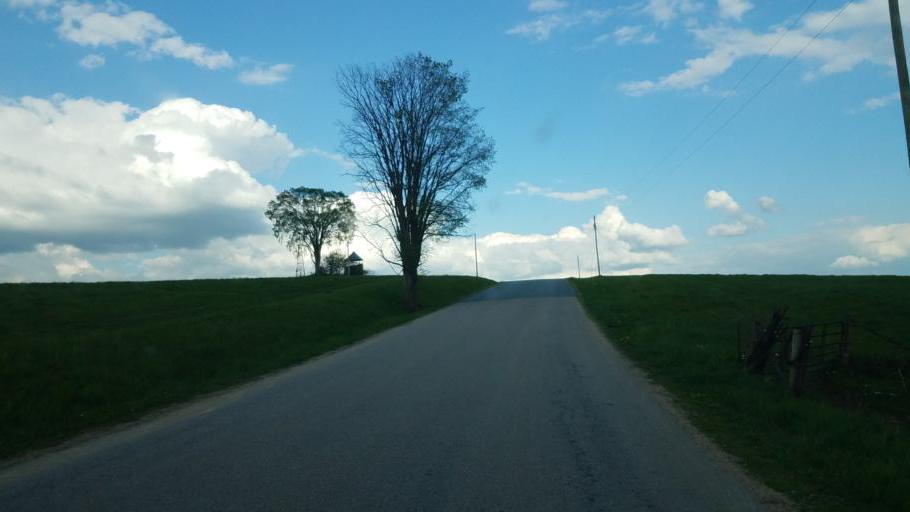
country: US
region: Wisconsin
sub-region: Vernon County
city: Hillsboro
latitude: 43.6856
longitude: -90.3852
